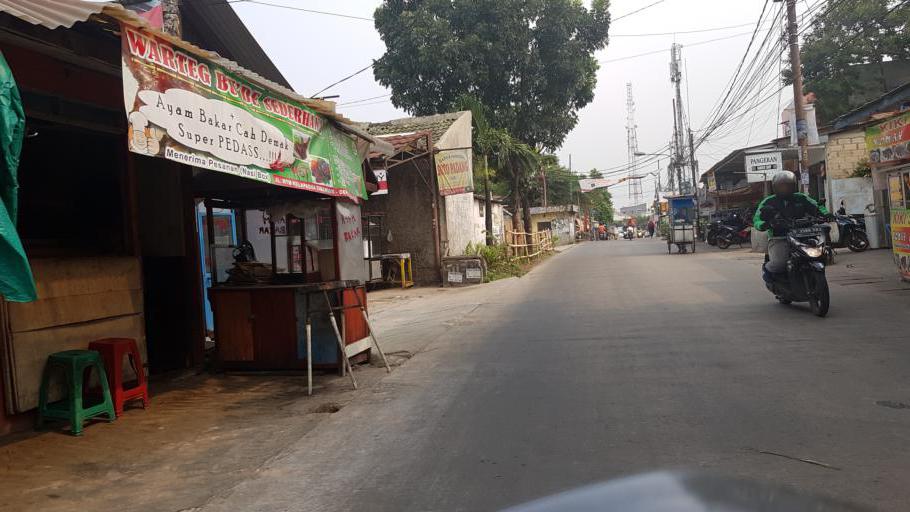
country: ID
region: West Java
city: Depok
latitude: -6.3576
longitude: 106.8430
